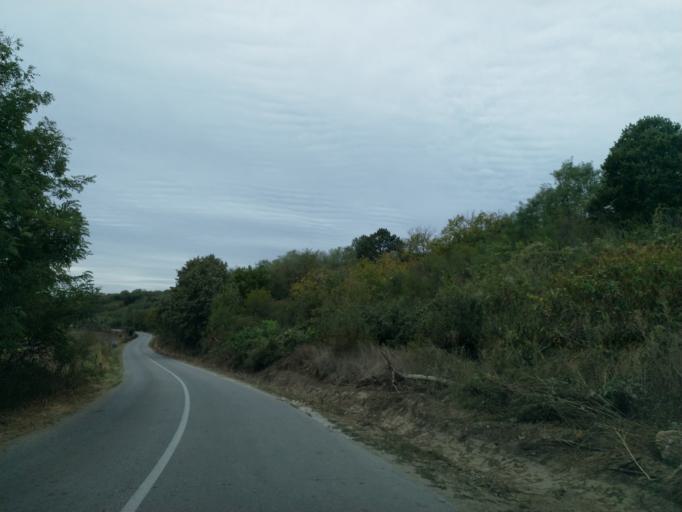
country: RS
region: Central Serbia
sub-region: Pomoravski Okrug
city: Paracin
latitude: 43.8513
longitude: 21.3228
